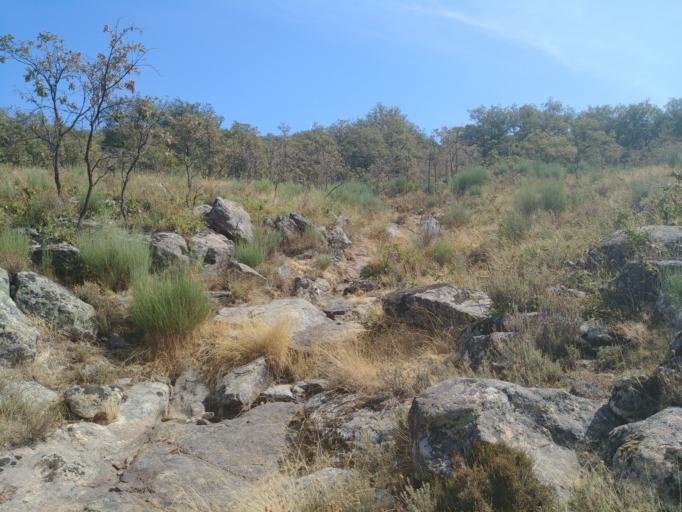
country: ES
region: Extremadura
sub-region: Provincia de Caceres
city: Garganta la Olla
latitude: 40.1096
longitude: -5.7664
